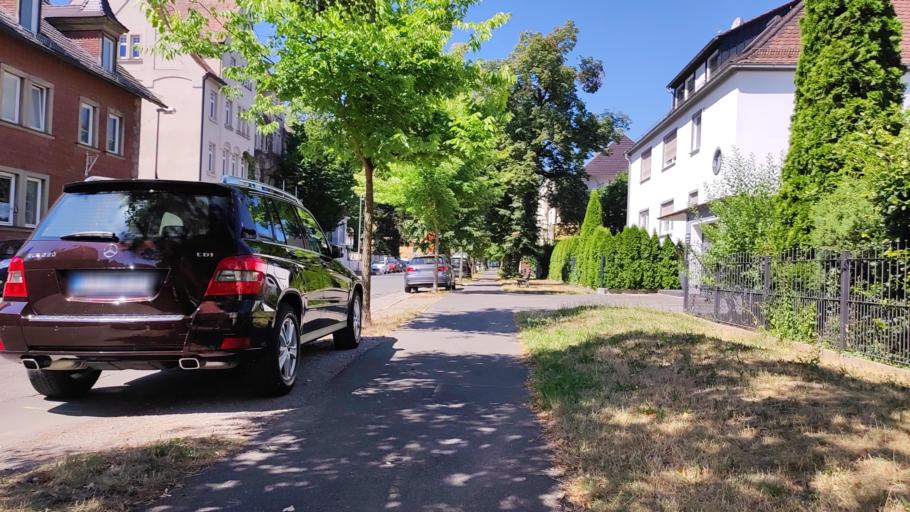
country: DE
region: Bavaria
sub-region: Regierungsbezirk Mittelfranken
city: Neustadt an der Aisch
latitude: 49.5773
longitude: 10.5994
